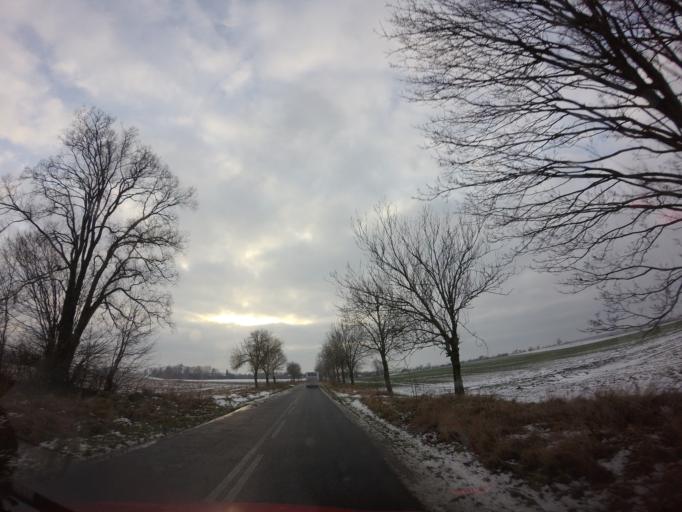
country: PL
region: West Pomeranian Voivodeship
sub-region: Powiat choszczenski
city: Krzecin
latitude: 53.0728
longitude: 15.4409
